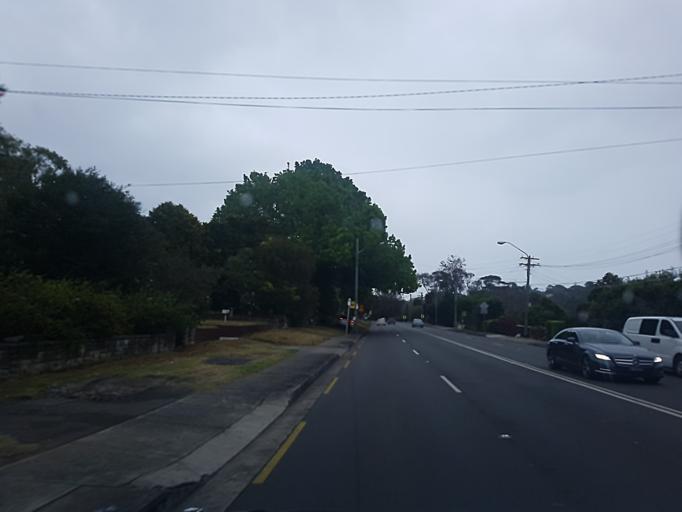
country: AU
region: New South Wales
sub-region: Willoughby
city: Castle Cove
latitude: -33.7893
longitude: 151.2068
